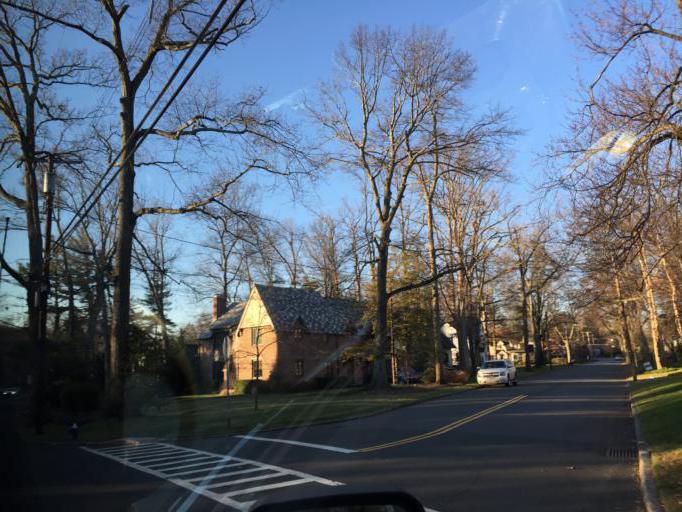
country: US
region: New Jersey
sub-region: Union County
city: New Providence
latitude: 40.7072
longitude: -74.3683
